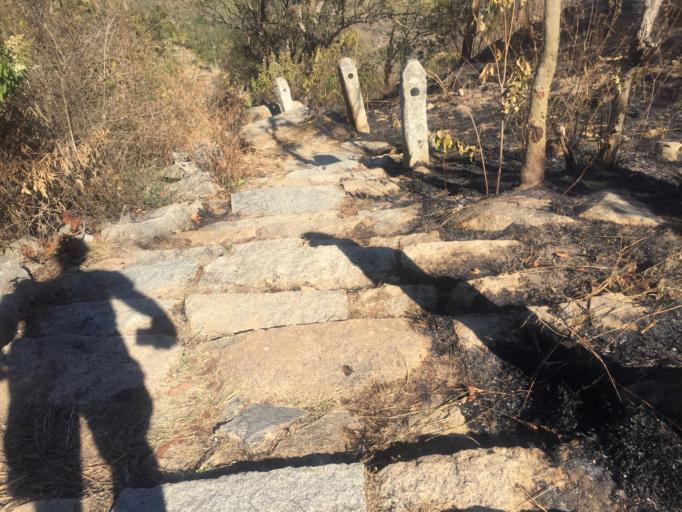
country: IN
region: Karnataka
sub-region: Chikkaballapur
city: Chik Ballapur
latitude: 13.3734
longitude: 77.6772
